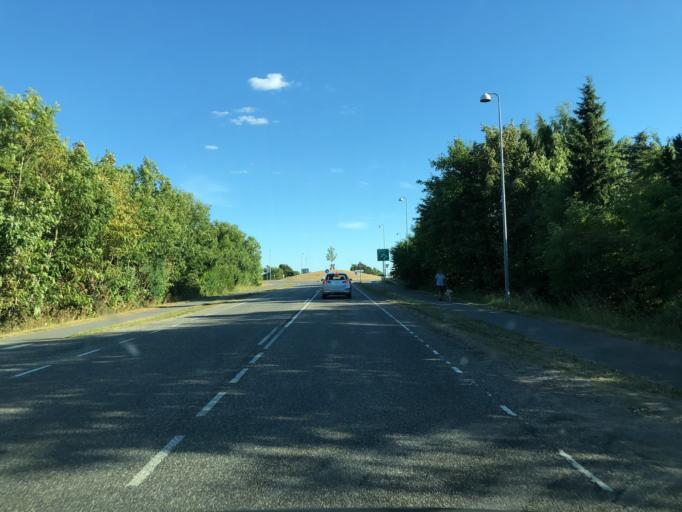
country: DK
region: Central Jutland
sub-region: Arhus Kommune
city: Framlev
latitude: 56.1556
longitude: 10.0066
